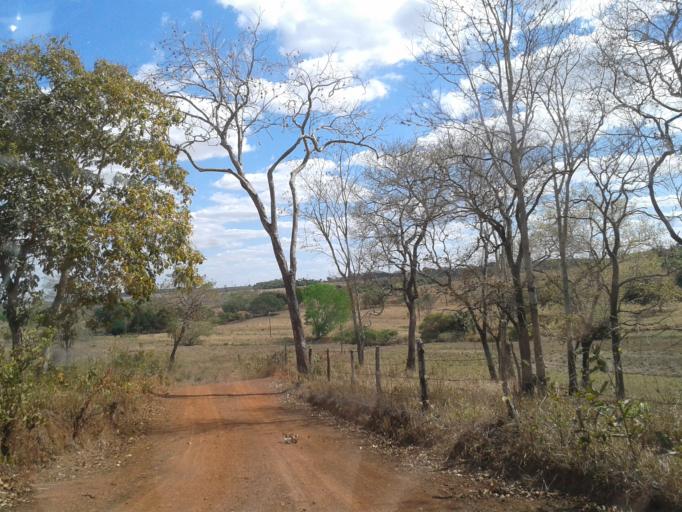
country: BR
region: Minas Gerais
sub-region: Monte Alegre De Minas
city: Monte Alegre de Minas
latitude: -18.7946
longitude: -49.0922
